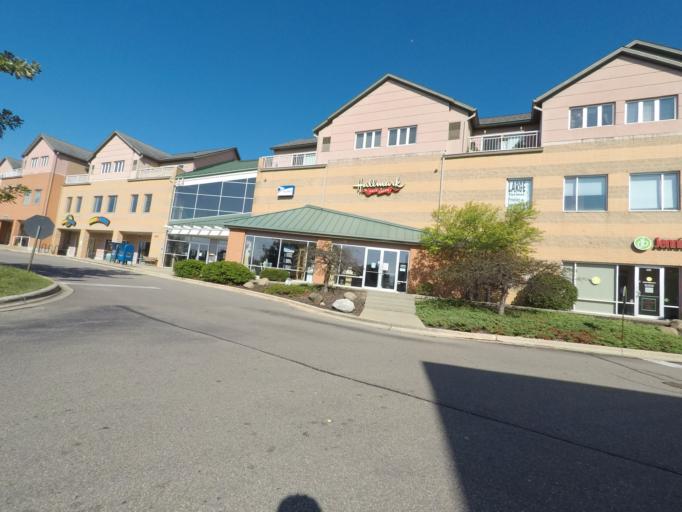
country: US
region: Wisconsin
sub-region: Dane County
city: Madison
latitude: 43.0185
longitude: -89.4220
